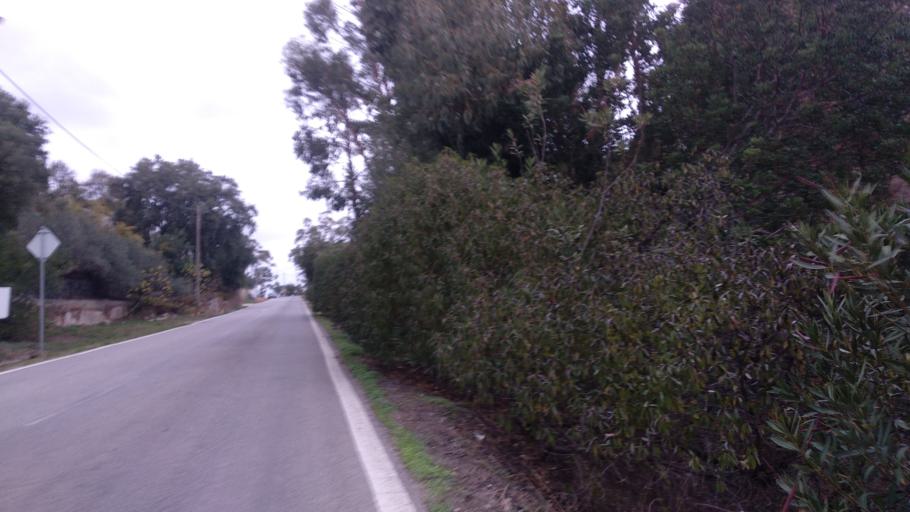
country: PT
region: Faro
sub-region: Sao Bras de Alportel
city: Sao Bras de Alportel
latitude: 37.1780
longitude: -7.9099
